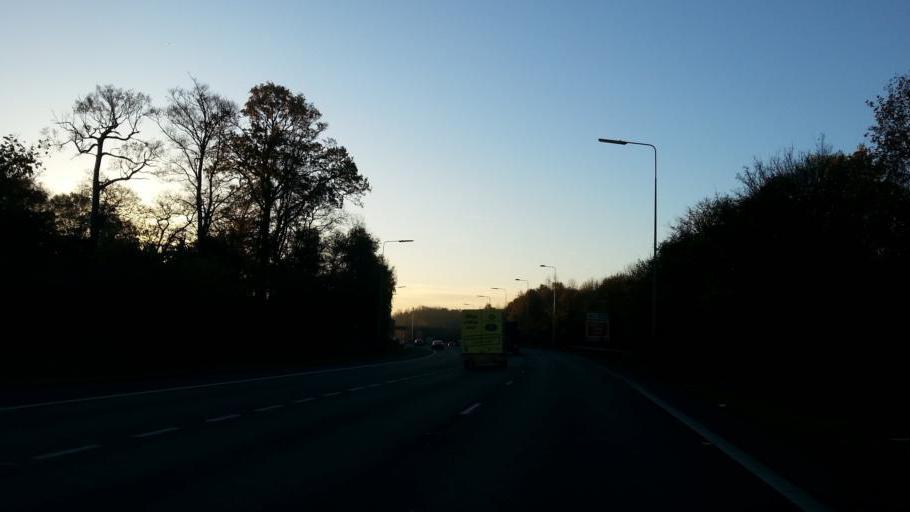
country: GB
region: England
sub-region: Hertfordshire
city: Abbots Langley
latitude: 51.7207
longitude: -0.3863
